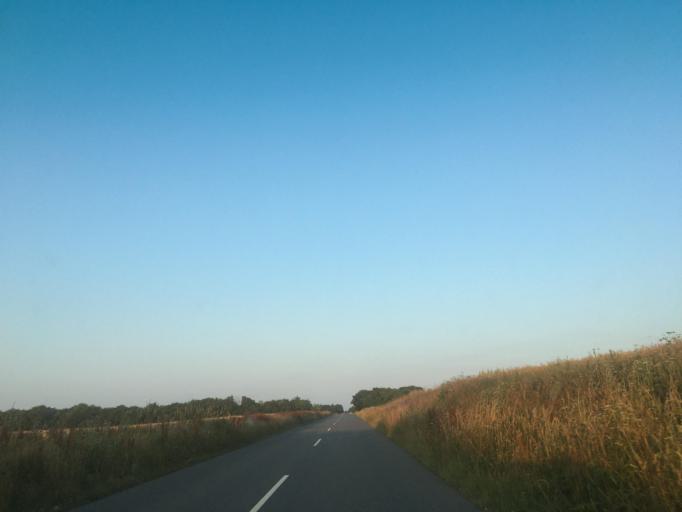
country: DK
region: North Denmark
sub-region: Thisted Kommune
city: Hurup
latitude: 56.7557
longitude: 8.3654
